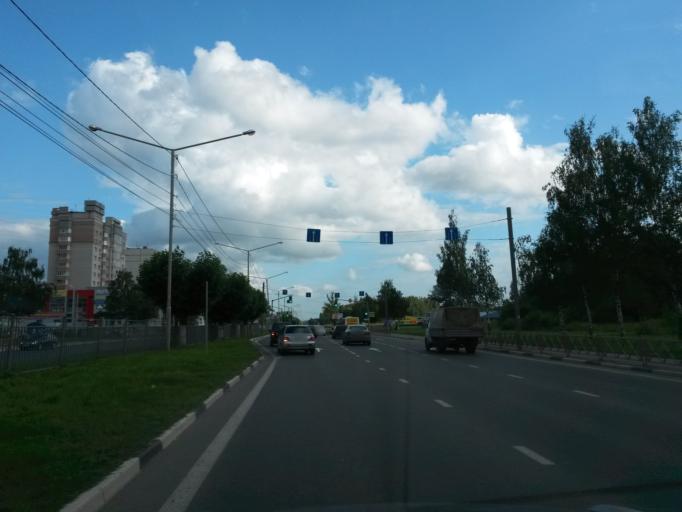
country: RU
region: Jaroslavl
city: Yaroslavl
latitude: 57.5815
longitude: 39.9107
